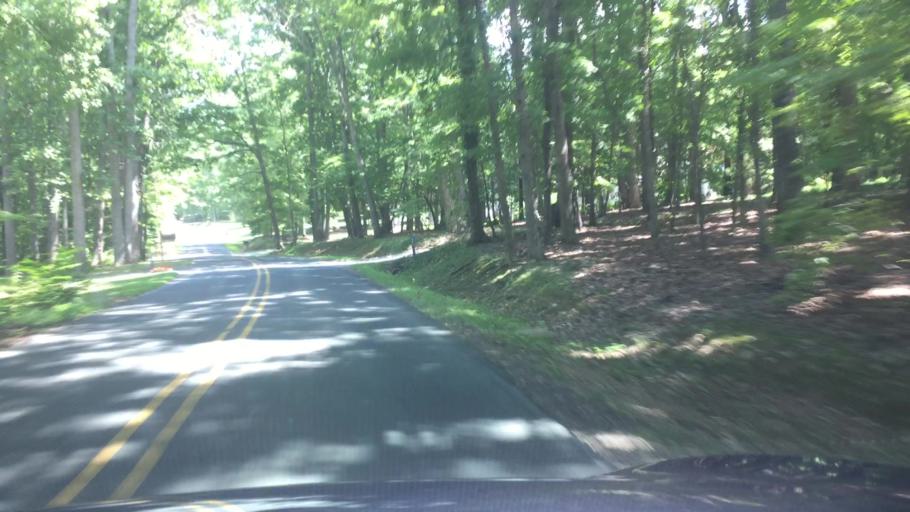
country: US
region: Virginia
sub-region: Appomattox County
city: Appomattox
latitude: 37.3303
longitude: -78.8774
